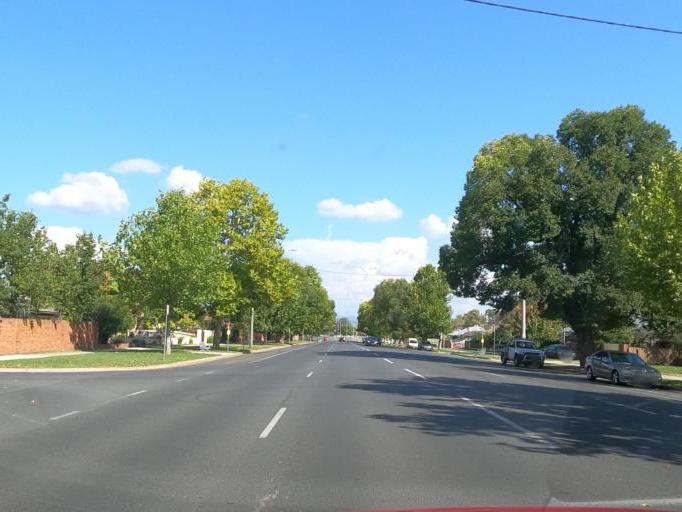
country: AU
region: New South Wales
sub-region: Albury Municipality
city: Albury
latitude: -36.0653
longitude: 146.9244
